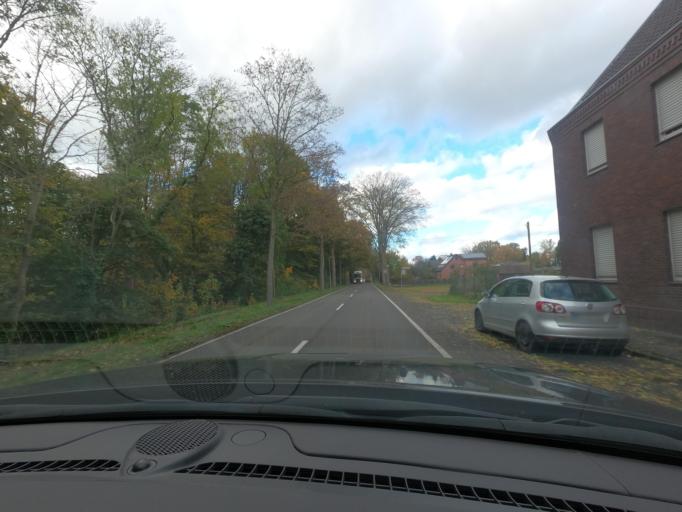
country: DE
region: North Rhine-Westphalia
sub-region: Regierungsbezirk Dusseldorf
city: Schwalmtal
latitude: 51.2579
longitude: 6.2924
